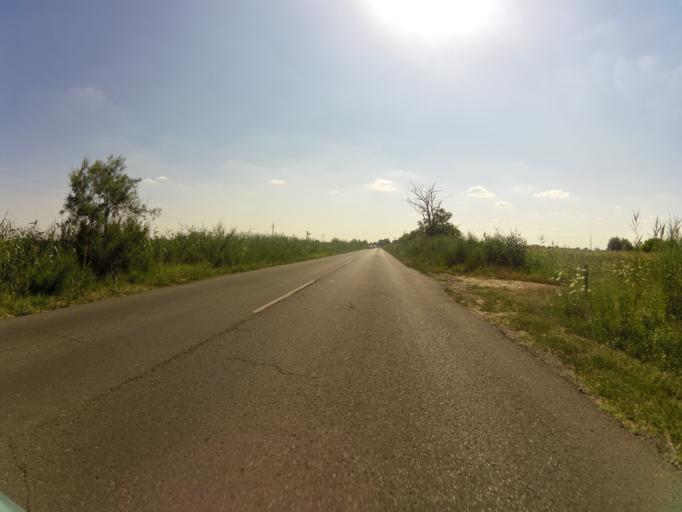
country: HU
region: Csongrad
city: Sandorfalva
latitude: 46.3562
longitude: 20.0729
